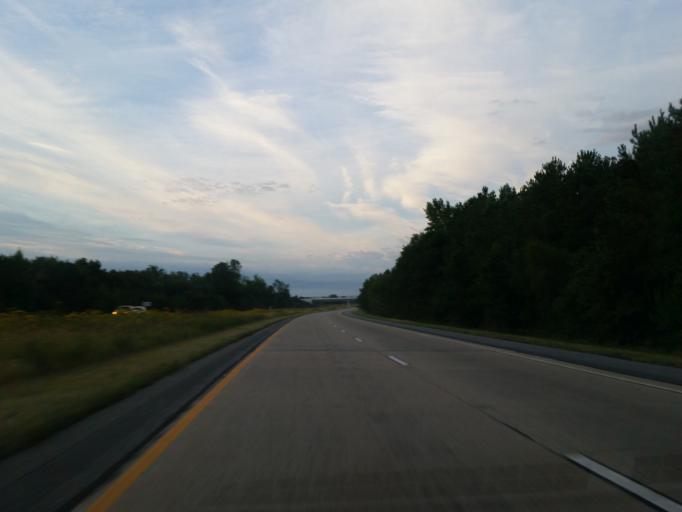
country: US
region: Delaware
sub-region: Kent County
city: Cheswold
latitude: 39.2594
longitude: -75.5786
